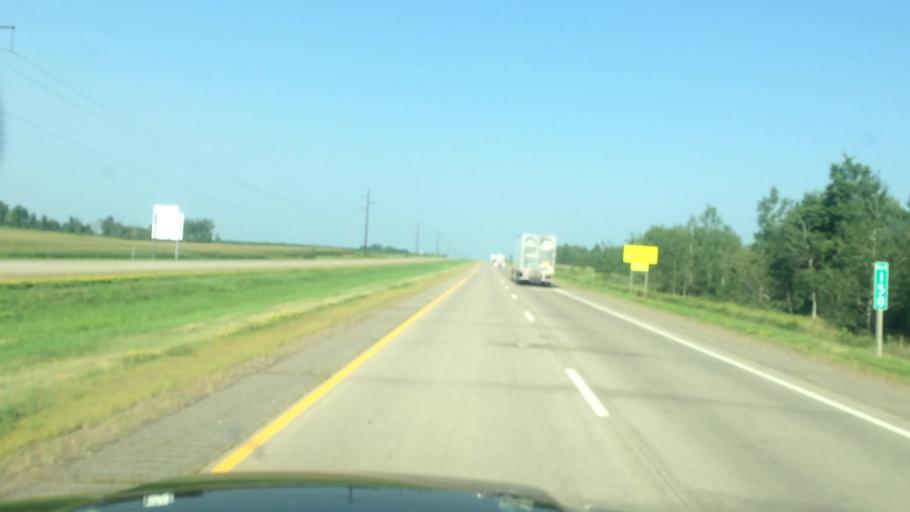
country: US
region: Wisconsin
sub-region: Marathon County
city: Edgar
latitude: 44.9445
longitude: -89.9783
